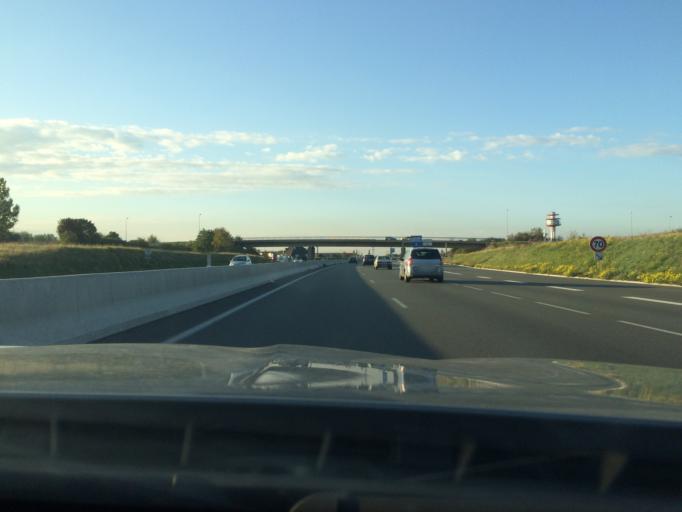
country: FR
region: Ile-de-France
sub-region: Departement de l'Essonne
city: Villabe
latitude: 48.5906
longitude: 2.4462
